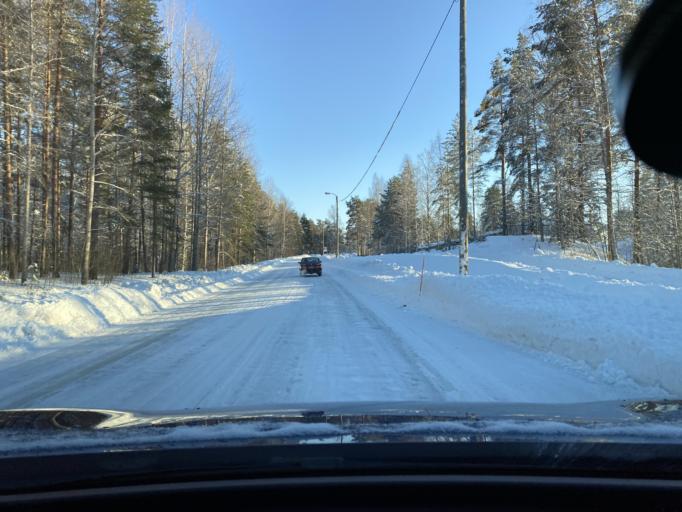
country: FI
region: Southern Savonia
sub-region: Mikkeli
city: Kangasniemi
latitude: 61.9945
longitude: 26.6317
